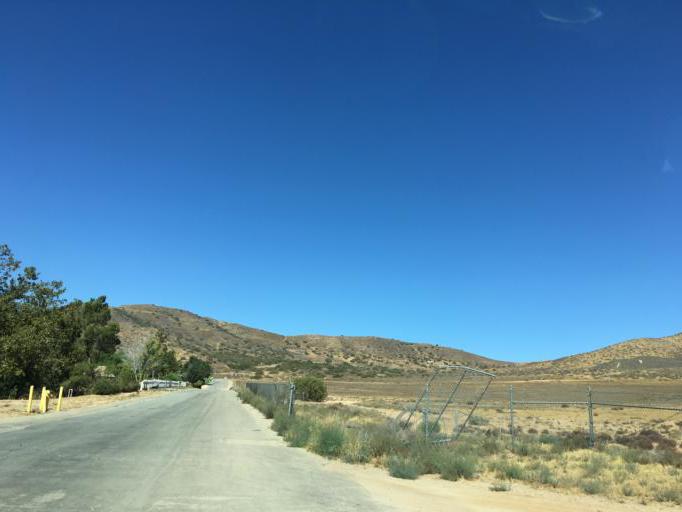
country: US
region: California
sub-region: Los Angeles County
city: Acton
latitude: 34.5061
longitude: -118.1939
